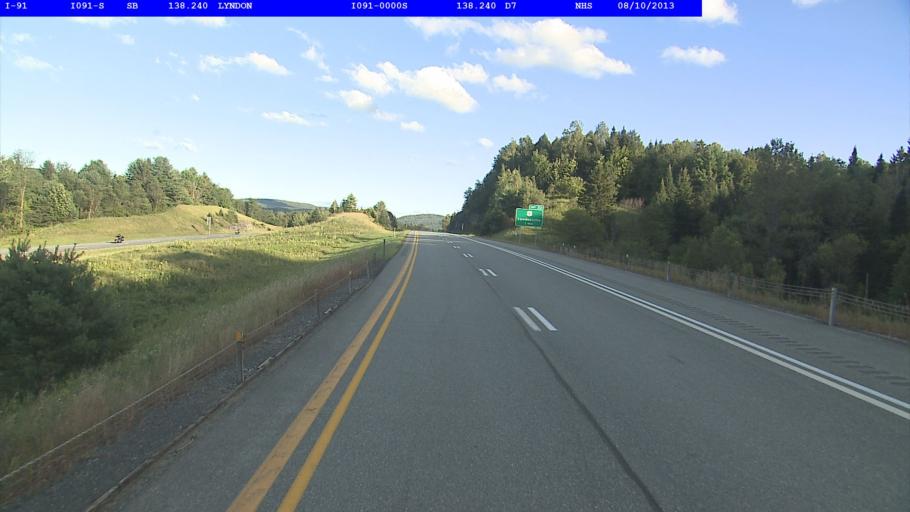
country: US
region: Vermont
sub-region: Caledonia County
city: Lyndonville
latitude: 44.5315
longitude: -72.0165
